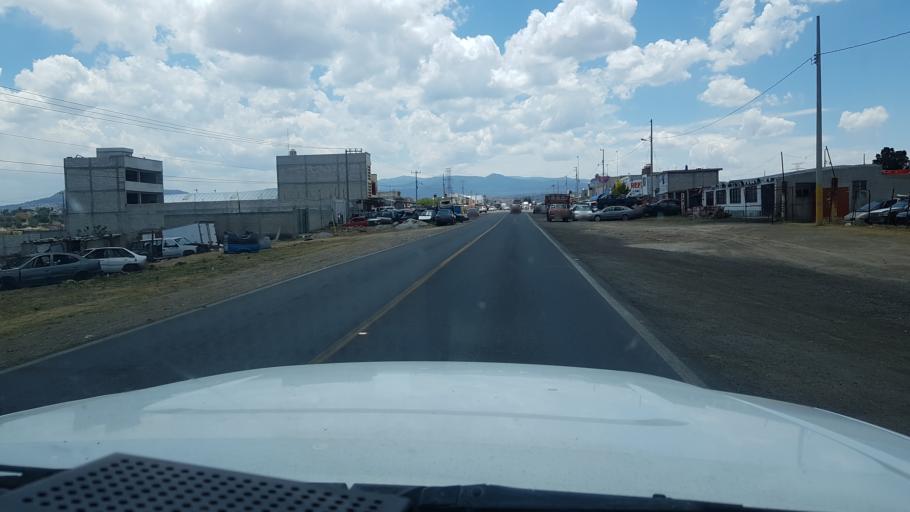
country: MX
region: Hidalgo
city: Calpulalpan
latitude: 19.6004
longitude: -98.5682
